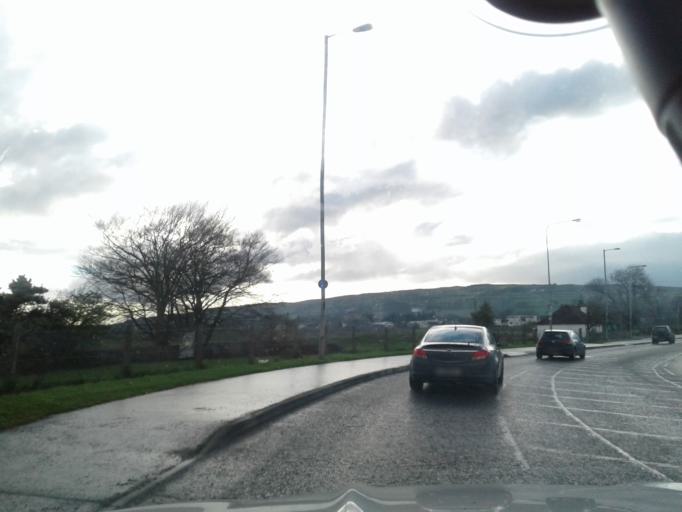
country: GB
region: Northern Ireland
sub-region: Strabane District
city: Strabane
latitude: 54.8295
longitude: -7.4734
